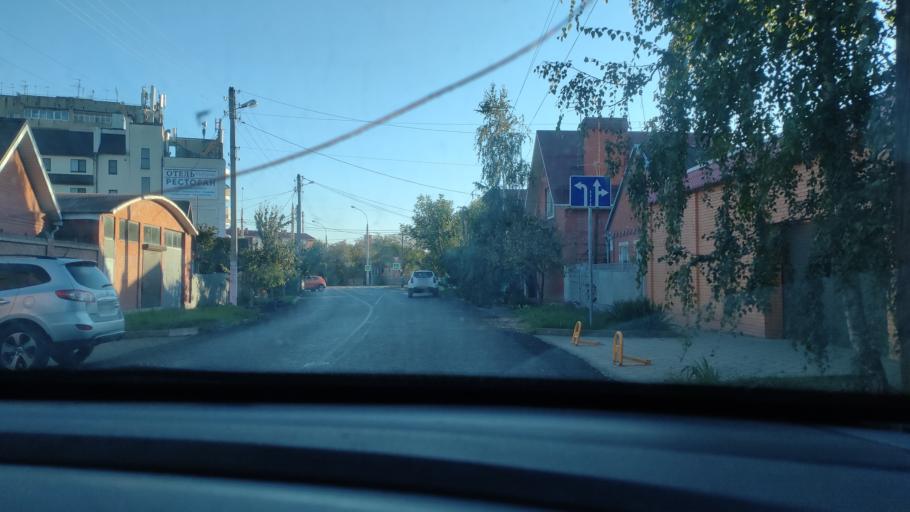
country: RU
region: Krasnodarskiy
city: Krasnodar
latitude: 45.0426
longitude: 38.9341
